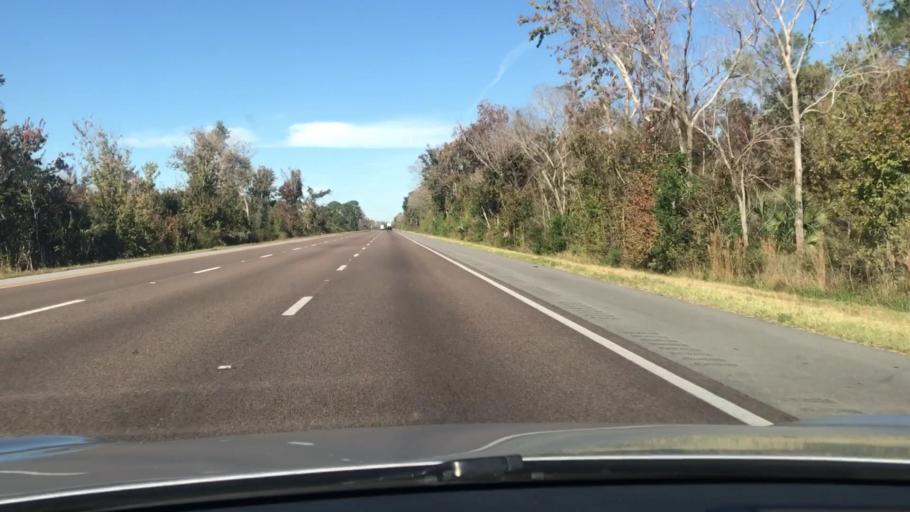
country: US
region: Florida
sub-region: Volusia County
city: Oak Hill
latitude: 28.8859
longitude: -80.9251
